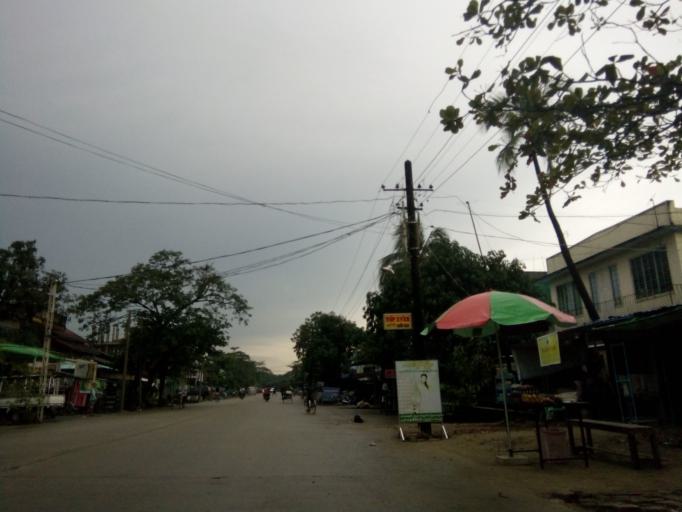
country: MM
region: Yangon
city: Yangon
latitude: 16.9148
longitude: 96.1607
